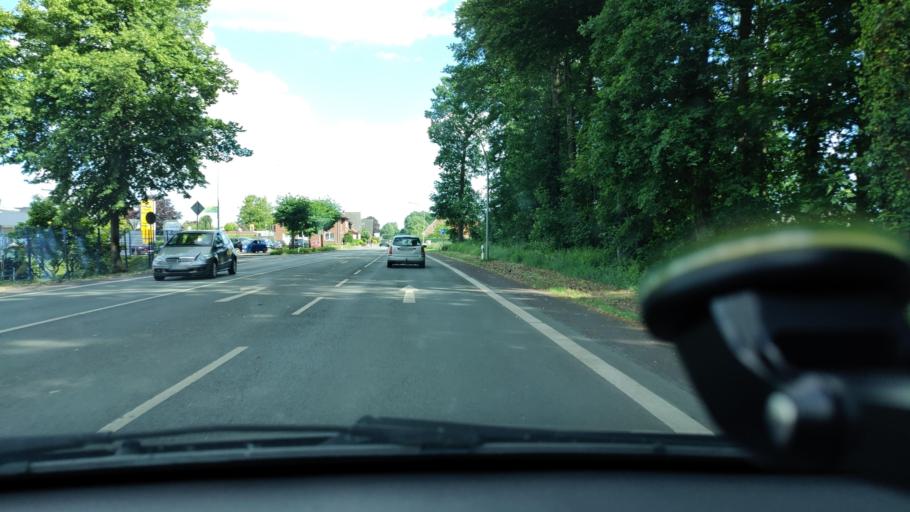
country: DE
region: North Rhine-Westphalia
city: Stadtlohn
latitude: 51.9890
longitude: 6.9375
